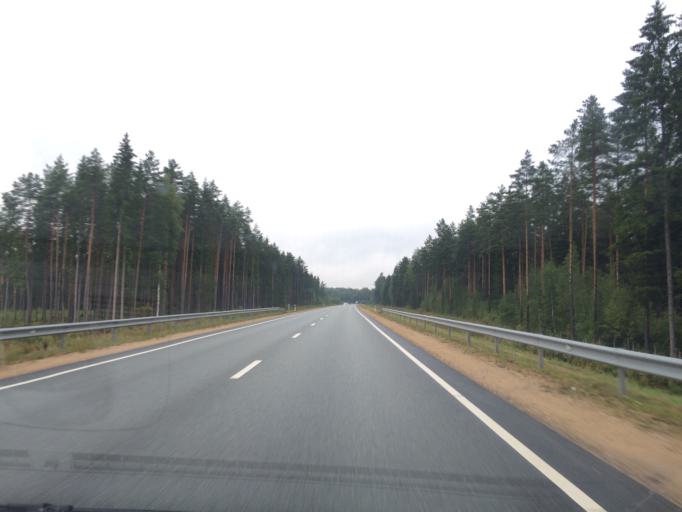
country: LV
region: Ogre
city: Ogre
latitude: 56.8530
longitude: 24.6530
